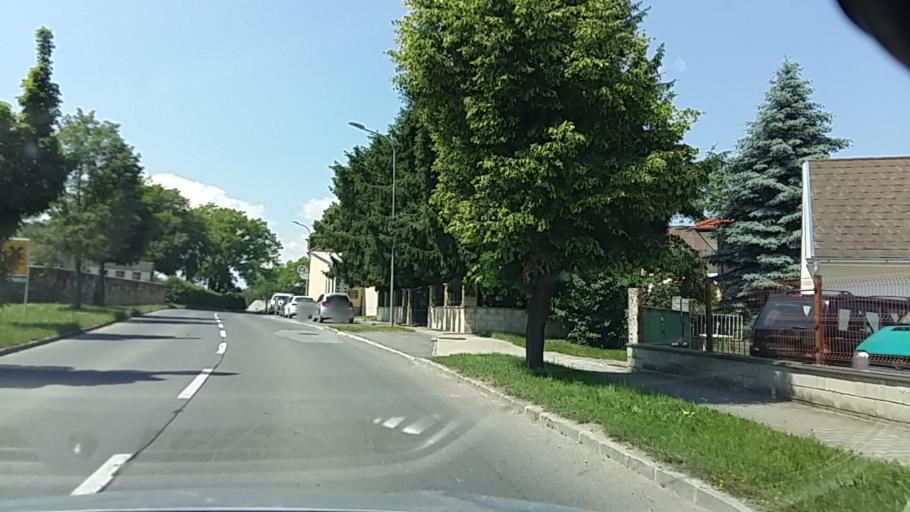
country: AT
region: Burgenland
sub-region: Politischer Bezirk Oberpullendorf
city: Horitschon
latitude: 47.5876
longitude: 16.5548
